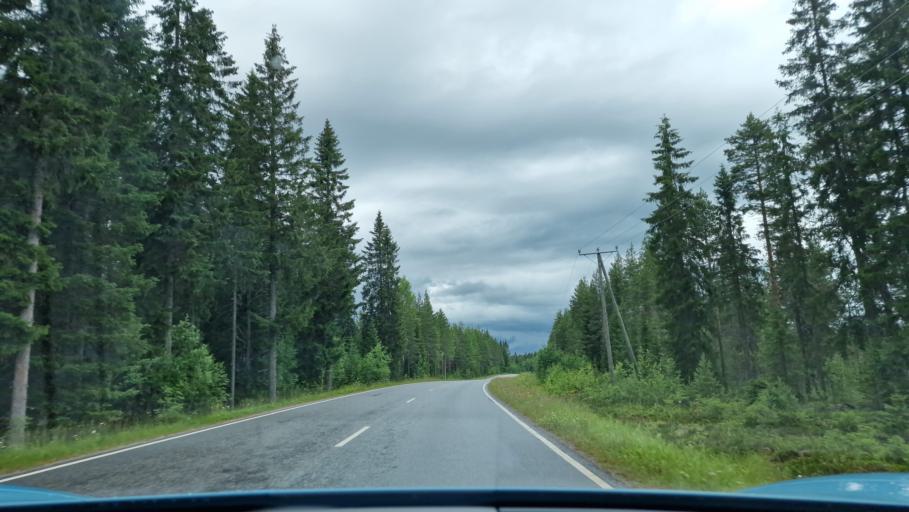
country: FI
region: Southern Ostrobothnia
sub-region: Jaerviseutu
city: Soini
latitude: 62.7224
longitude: 24.4262
